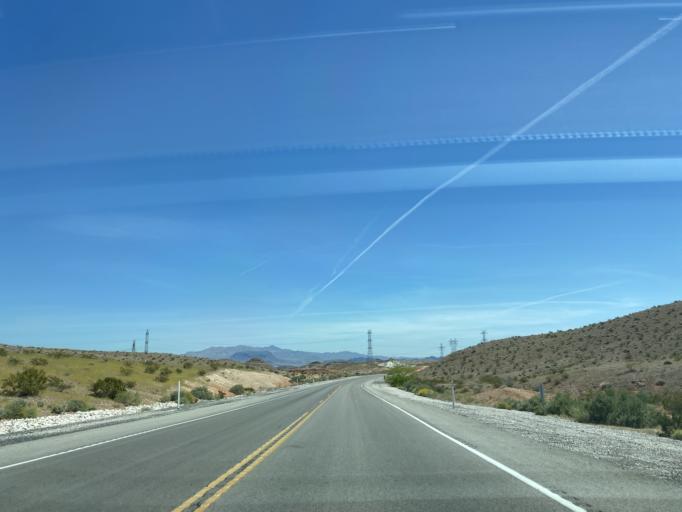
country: US
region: Nevada
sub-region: Clark County
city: Nellis Air Force Base
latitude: 36.1930
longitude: -114.9224
